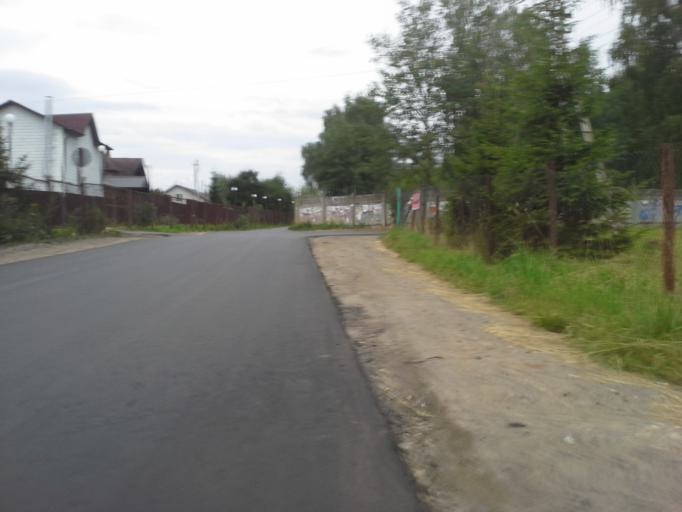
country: RU
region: Moscow
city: Tolstopal'tsevo
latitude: 55.6109
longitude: 37.2209
